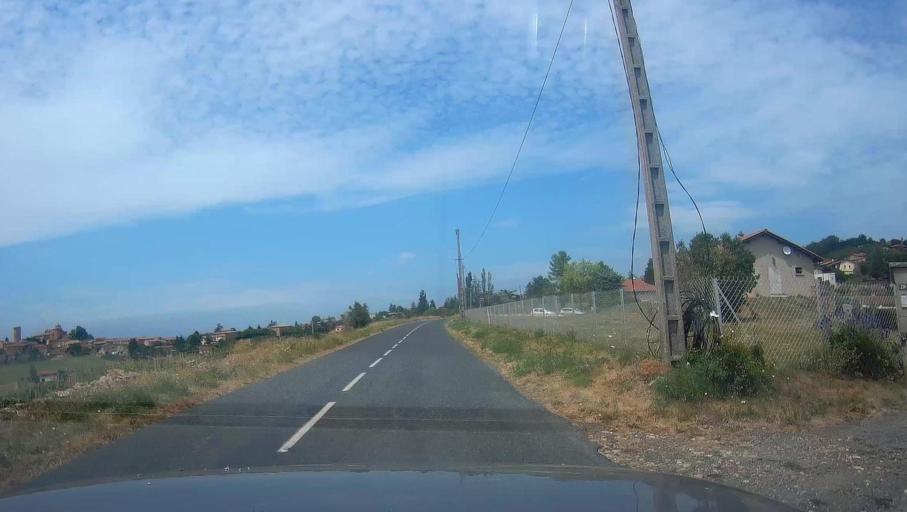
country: FR
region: Rhone-Alpes
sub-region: Departement du Rhone
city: Theize
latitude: 45.9458
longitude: 4.5910
